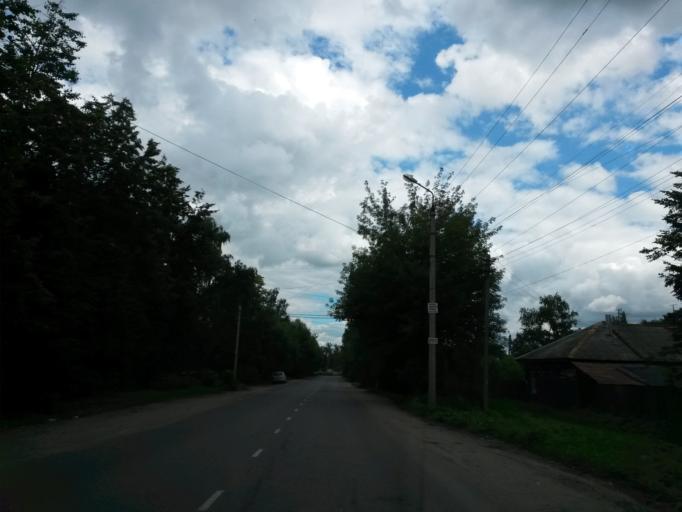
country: RU
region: Jaroslavl
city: Yaroslavl
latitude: 57.6063
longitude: 39.8812
